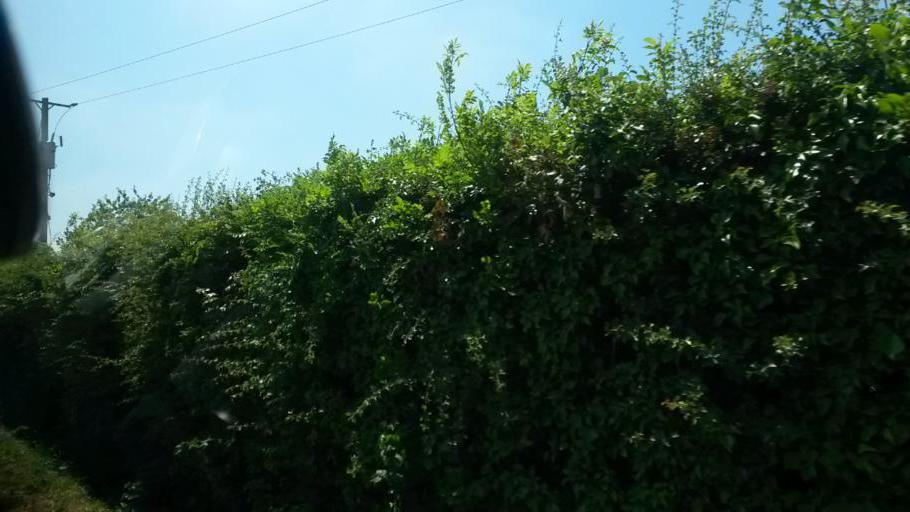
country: IE
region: Leinster
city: Lusk
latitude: 53.5317
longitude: -6.2365
